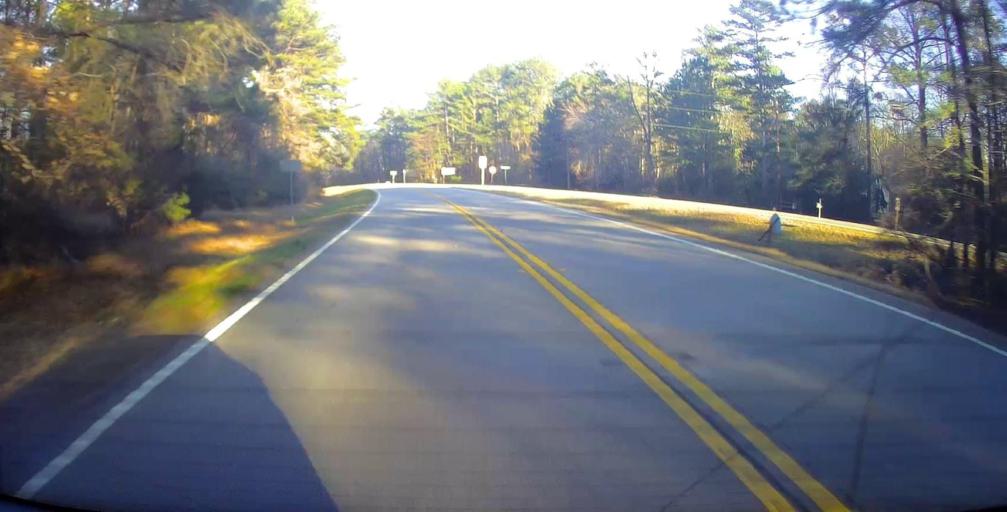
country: US
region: Georgia
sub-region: Harris County
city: Pine Mountain
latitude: 32.8444
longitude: -84.9002
